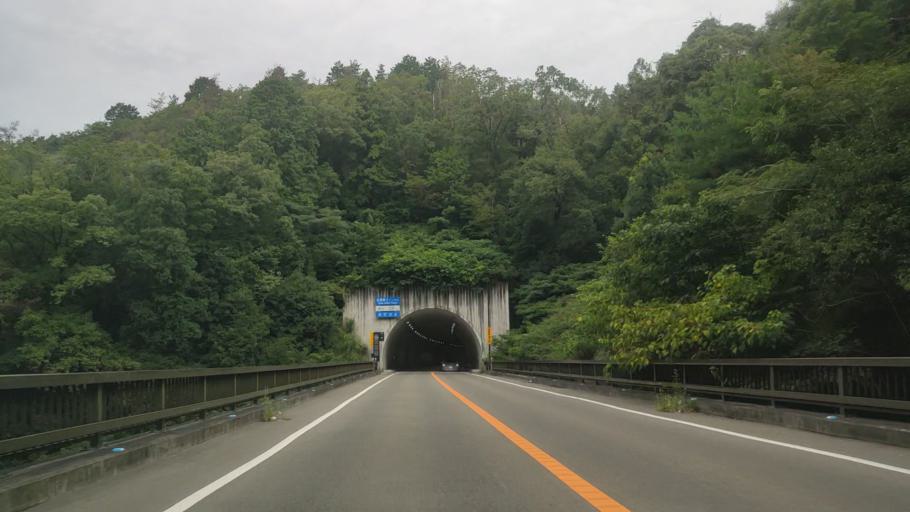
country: JP
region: Wakayama
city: Hashimoto
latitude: 34.4055
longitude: 135.5937
